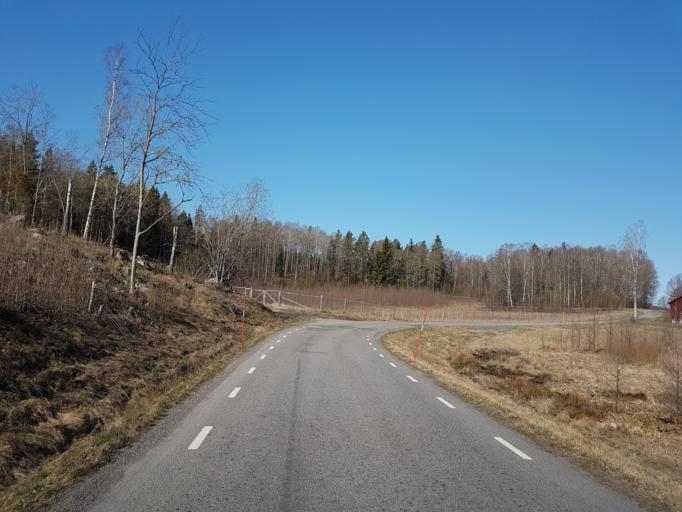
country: SE
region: OEstergoetland
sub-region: Valdemarsviks Kommun
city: Gusum
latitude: 58.1903
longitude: 16.2953
